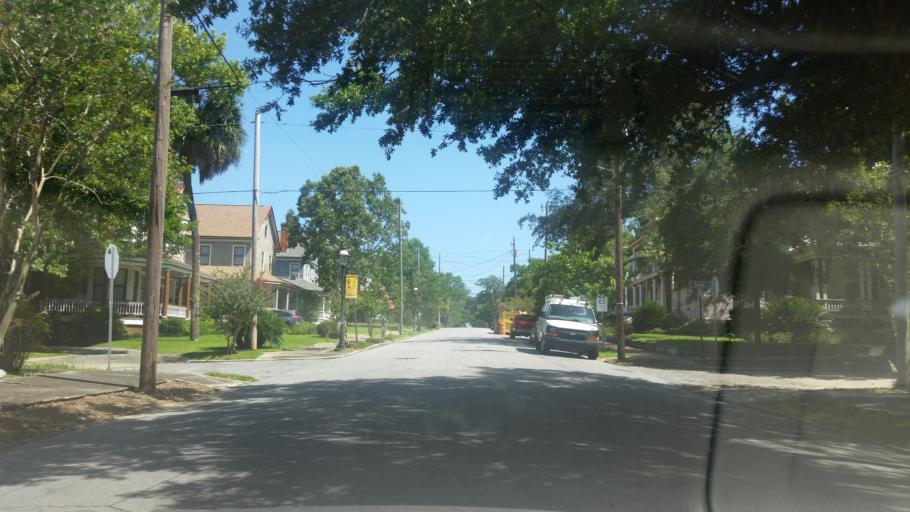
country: US
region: Florida
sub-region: Escambia County
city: Pensacola
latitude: 30.4216
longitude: -87.2202
